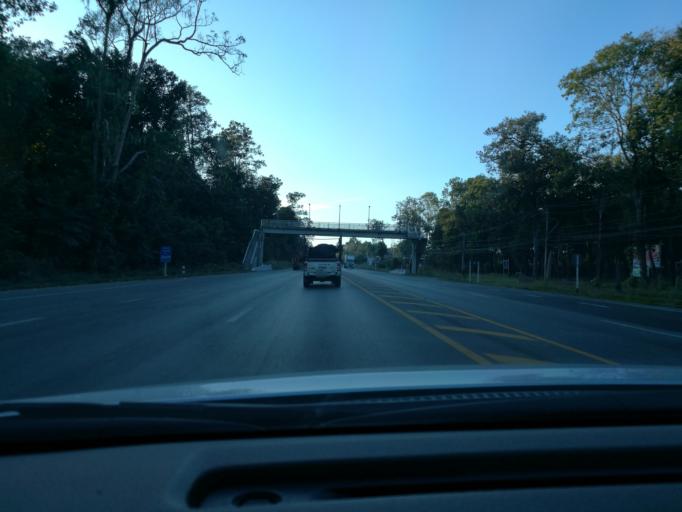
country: TH
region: Phitsanulok
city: Wang Thong
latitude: 16.8439
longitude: 100.5311
